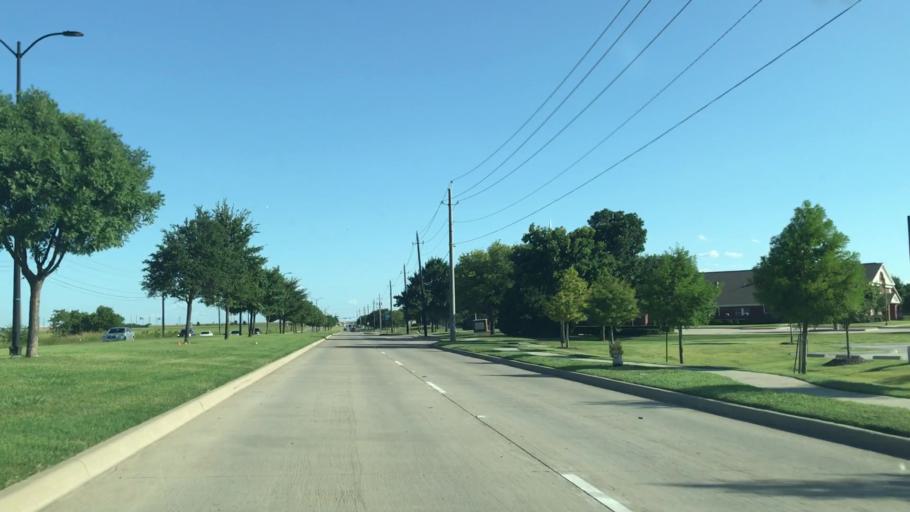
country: US
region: Texas
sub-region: Collin County
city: Frisco
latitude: 33.1217
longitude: -96.7681
